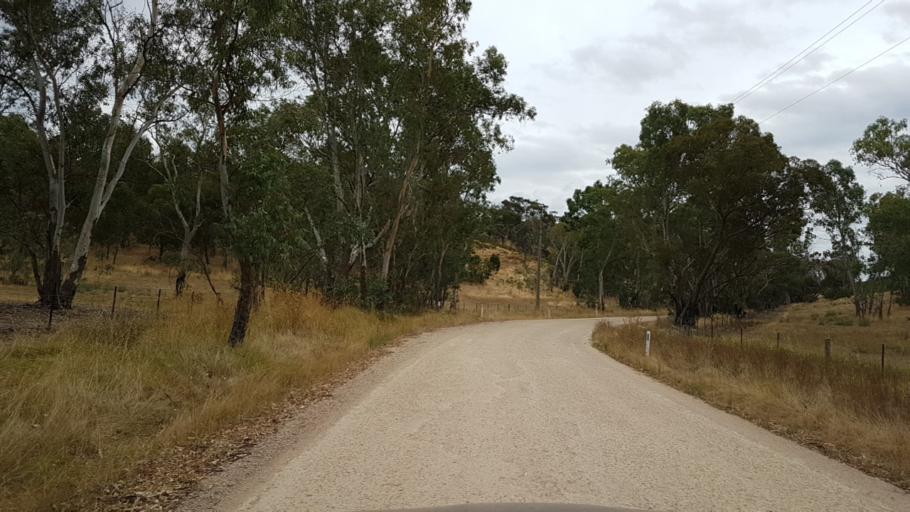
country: AU
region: South Australia
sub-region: Adelaide Hills
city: Gumeracha
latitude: -34.8072
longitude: 138.8340
